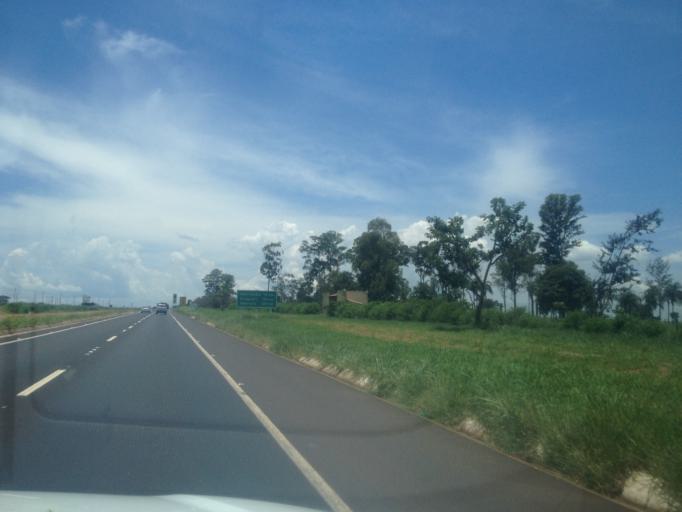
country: BR
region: Minas Gerais
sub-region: Uberlandia
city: Uberlandia
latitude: -18.8915
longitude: -48.4260
